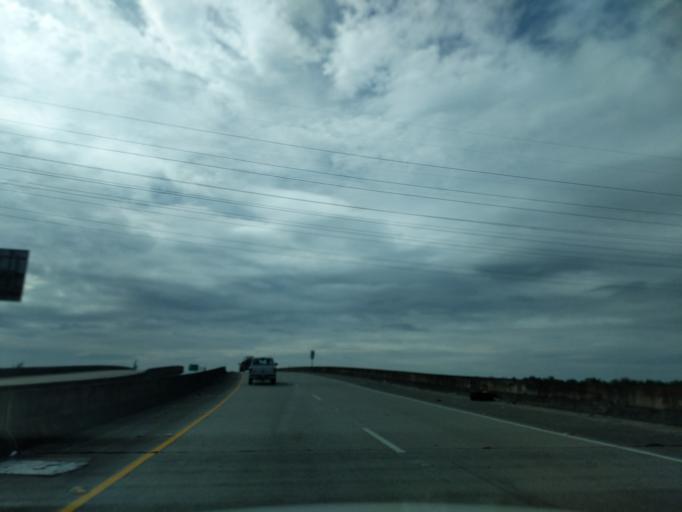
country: US
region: Louisiana
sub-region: Saint Bernard Parish
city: Chalmette
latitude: 30.0178
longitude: -89.9376
